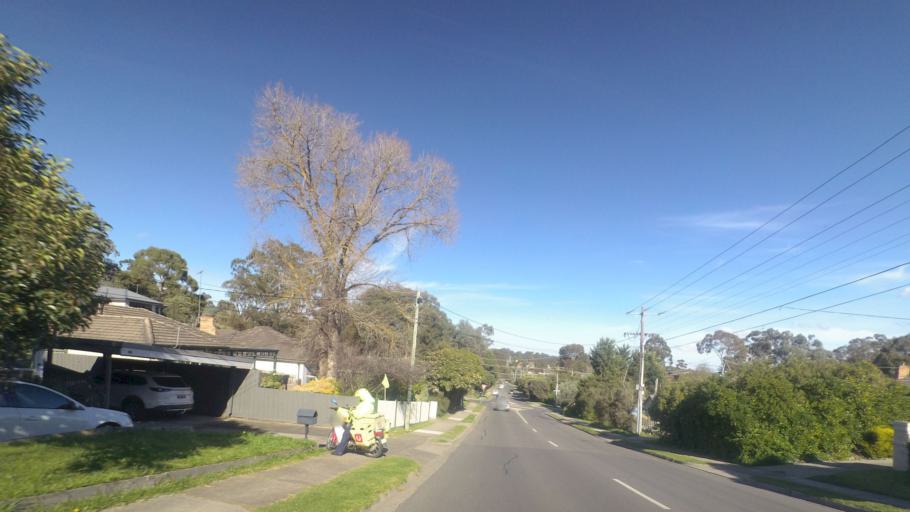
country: AU
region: Victoria
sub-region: Nillumbik
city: Eltham
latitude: -37.7188
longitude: 145.1511
